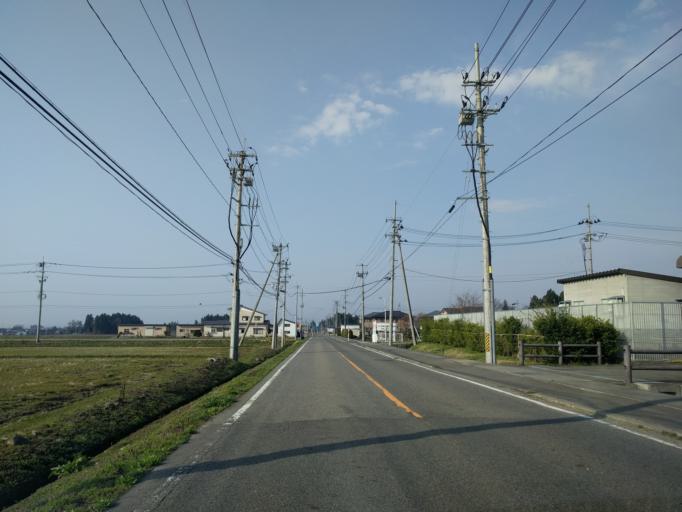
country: JP
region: Fukushima
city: Kitakata
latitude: 37.6741
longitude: 139.8923
